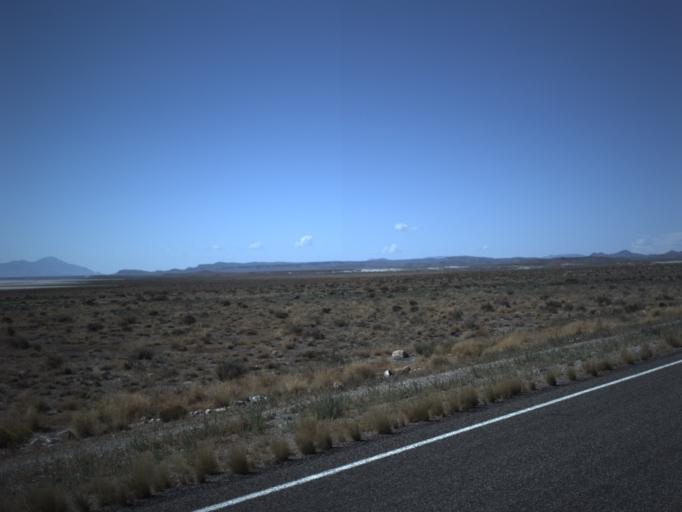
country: US
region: Utah
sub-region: Millard County
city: Delta
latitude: 39.0788
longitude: -113.2013
